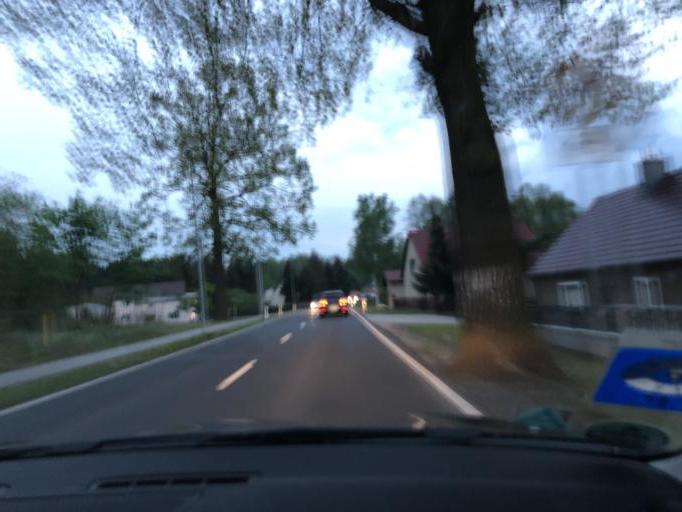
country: PL
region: Lubusz
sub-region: Powiat zarski
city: Leknica
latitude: 51.5250
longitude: 14.7273
